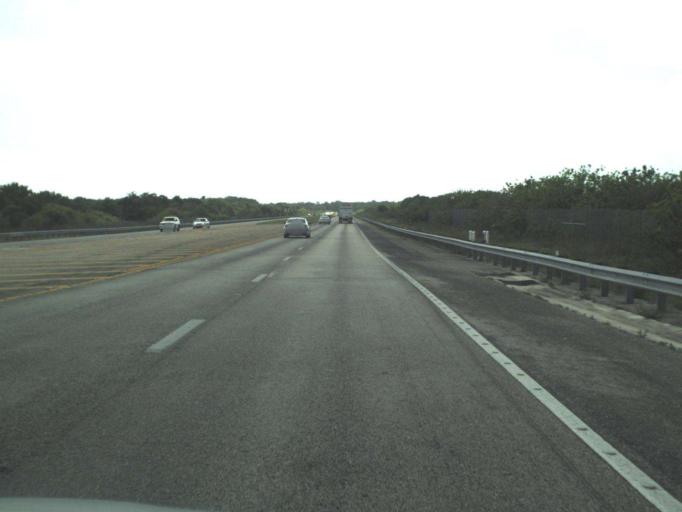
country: US
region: Florida
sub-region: Brevard County
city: Cocoa West
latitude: 28.3699
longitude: -80.8771
